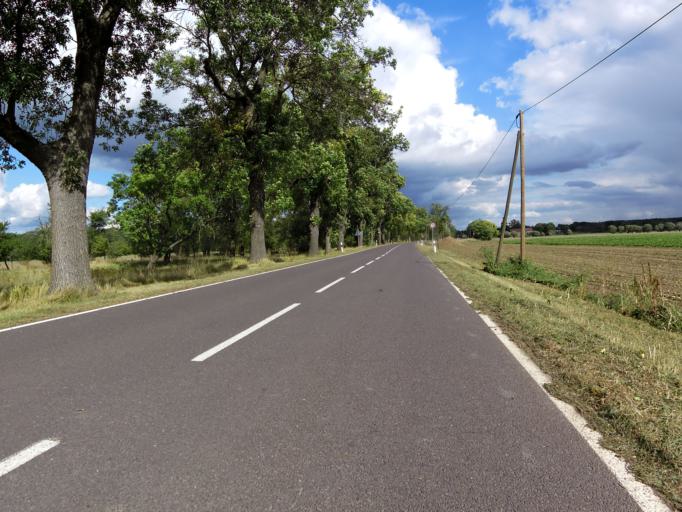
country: DE
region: Saxony-Anhalt
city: Barby
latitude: 51.9612
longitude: 11.9267
